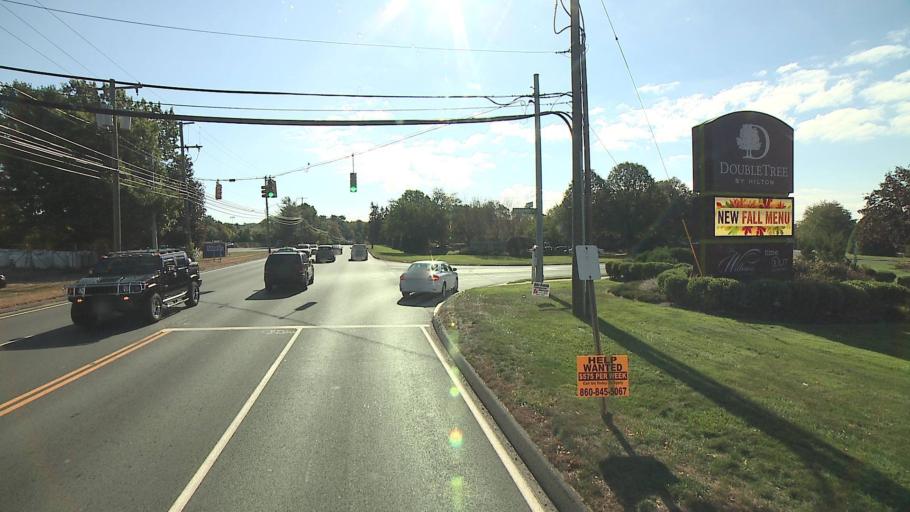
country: US
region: Connecticut
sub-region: Hartford County
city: Bristol
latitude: 41.6538
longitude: -72.9113
